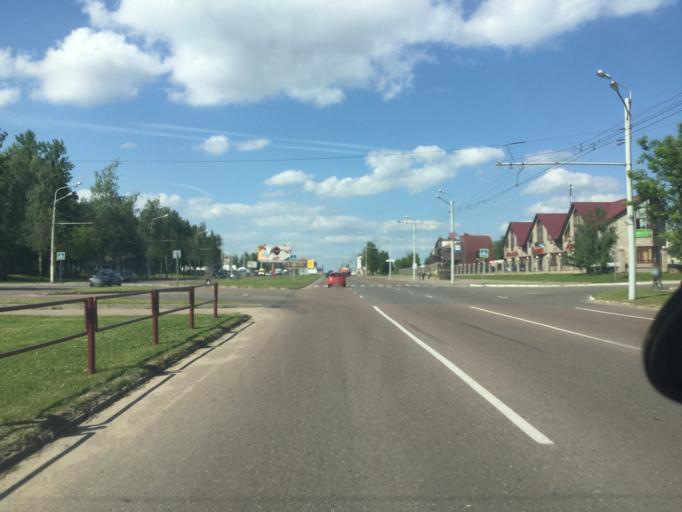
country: BY
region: Vitebsk
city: Vitebsk
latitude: 55.1783
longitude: 30.2459
